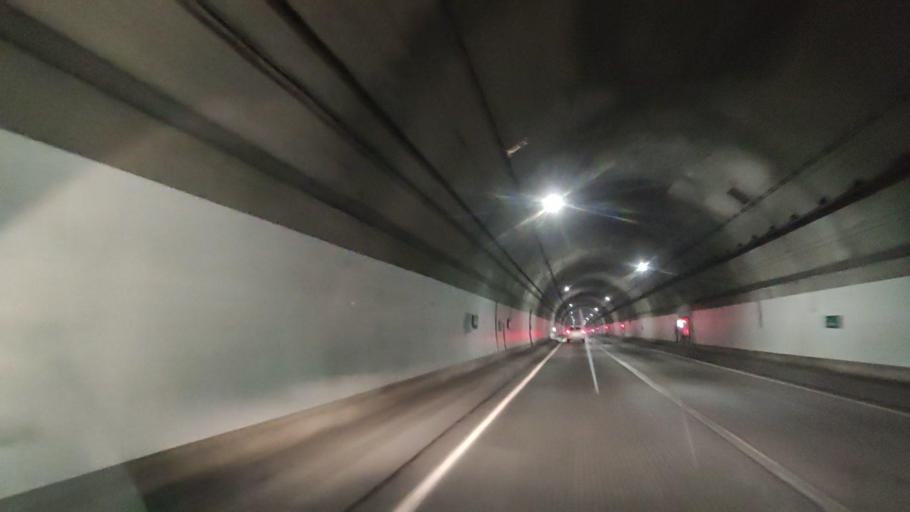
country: JP
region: Hokkaido
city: Rumoi
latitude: 43.7092
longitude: 141.3330
